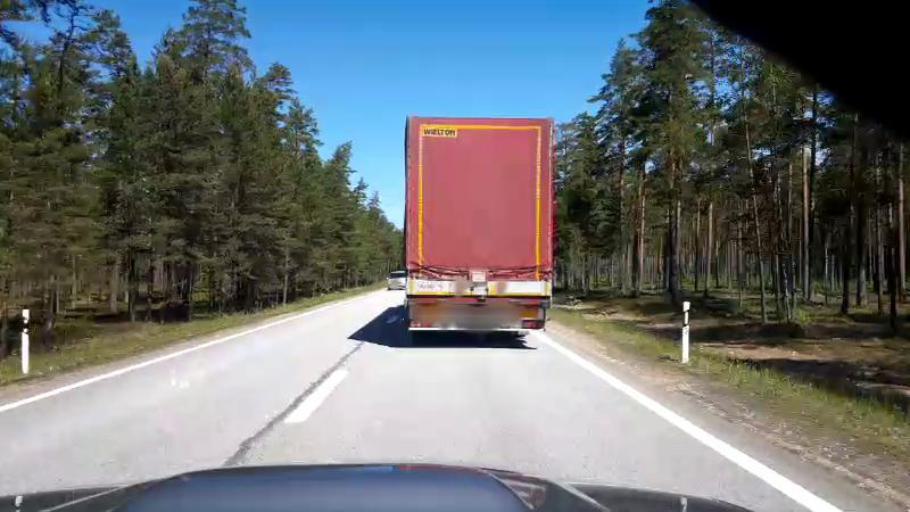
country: LV
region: Salacgrivas
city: Salacgriva
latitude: 57.5496
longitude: 24.4328
